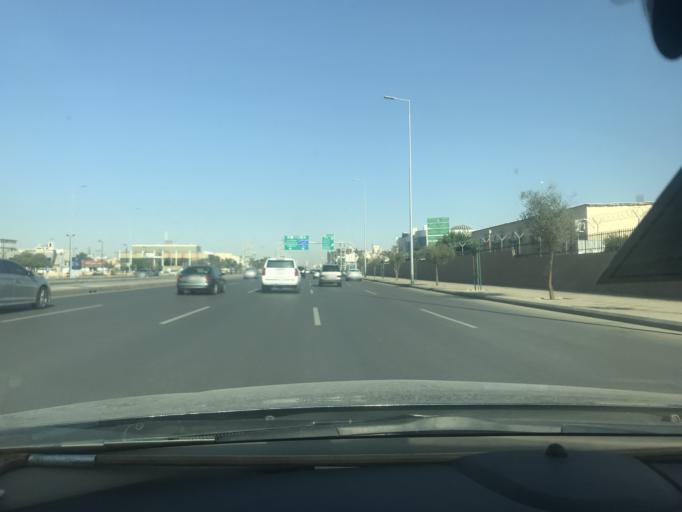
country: SA
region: Ar Riyad
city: Riyadh
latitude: 24.7439
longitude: 46.6818
